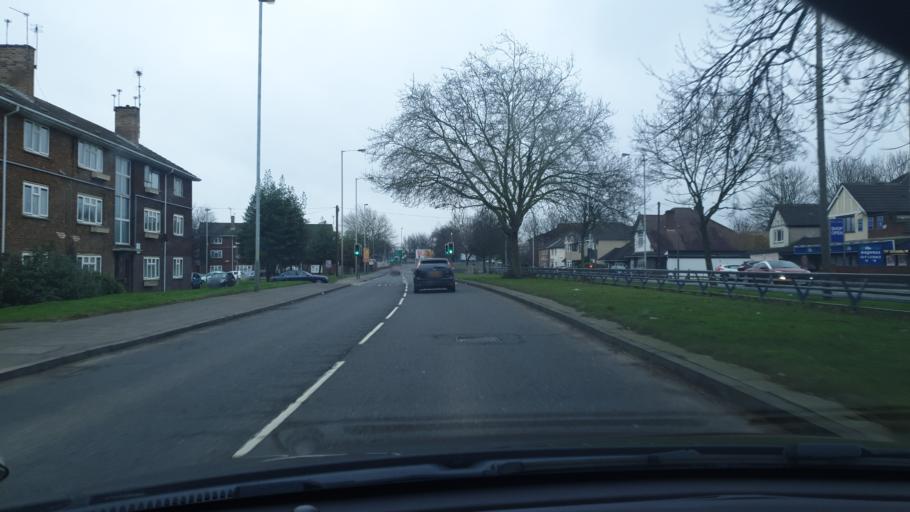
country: GB
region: England
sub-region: Walsall
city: Willenhall
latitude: 52.5835
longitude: -2.0717
